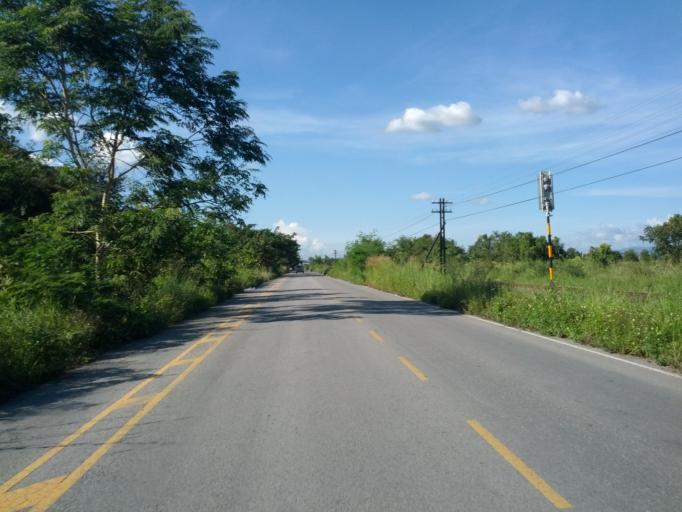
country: TH
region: Chiang Mai
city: Saraphi
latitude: 18.7261
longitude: 99.0348
